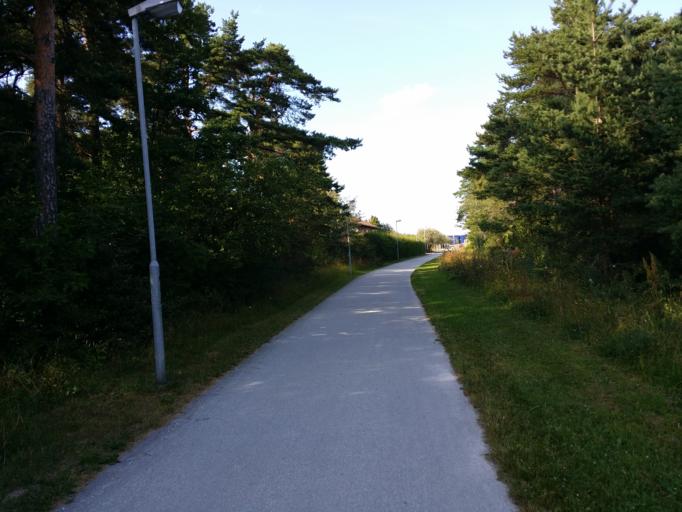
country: SE
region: Gotland
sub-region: Gotland
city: Visby
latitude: 57.6290
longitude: 18.3233
